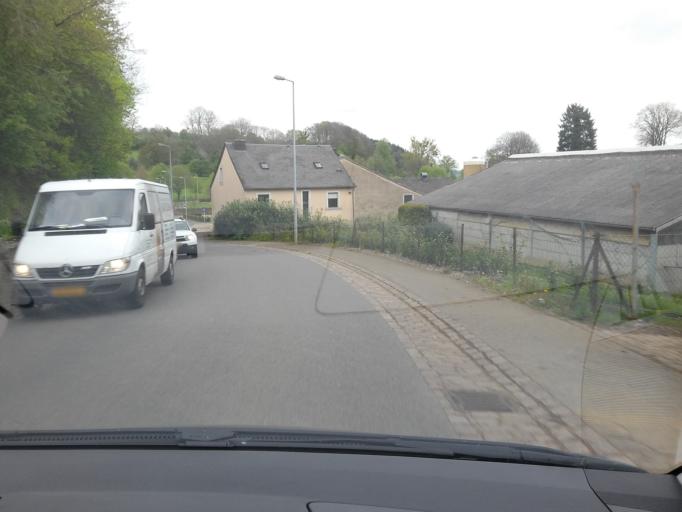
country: LU
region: Luxembourg
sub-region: Canton de Capellen
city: Garnich
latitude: 49.6056
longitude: 5.9303
